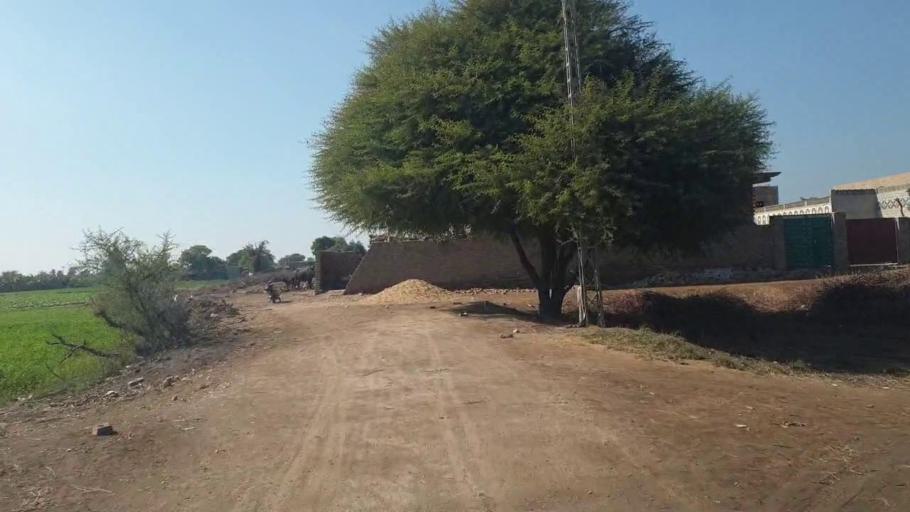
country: PK
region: Sindh
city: Shahdadpur
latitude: 25.9324
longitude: 68.5837
